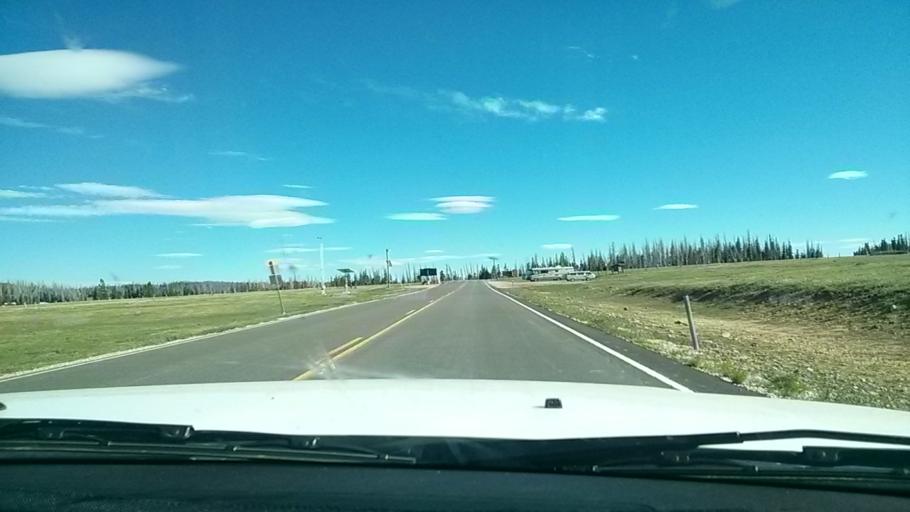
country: US
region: Utah
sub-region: Iron County
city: Parowan
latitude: 37.6642
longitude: -112.8379
